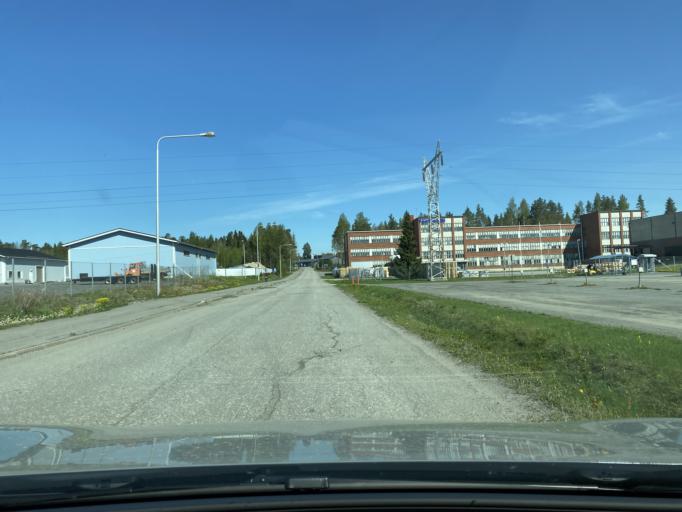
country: FI
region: Pirkanmaa
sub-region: Lounais-Pirkanmaa
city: Vammala
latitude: 61.3514
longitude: 22.8813
